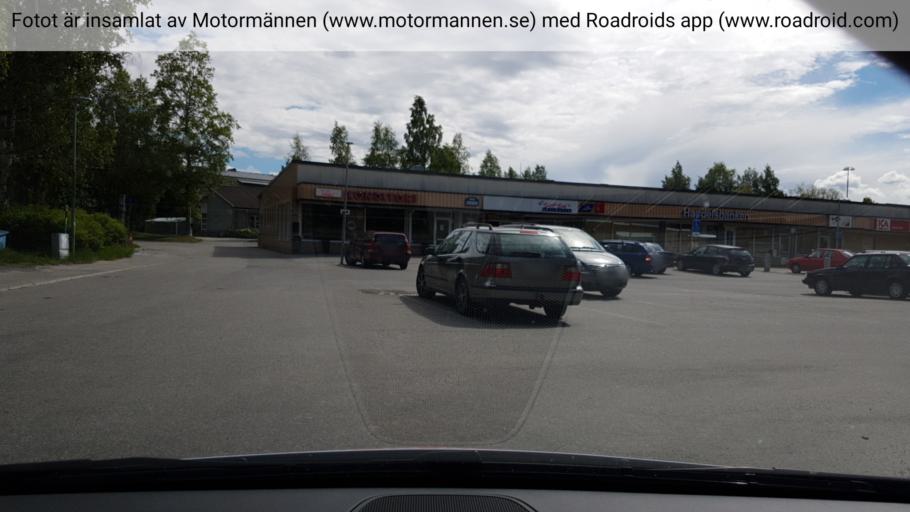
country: SE
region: Vaesterbotten
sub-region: Umea Kommun
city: Umea
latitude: 63.8368
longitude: 20.2335
